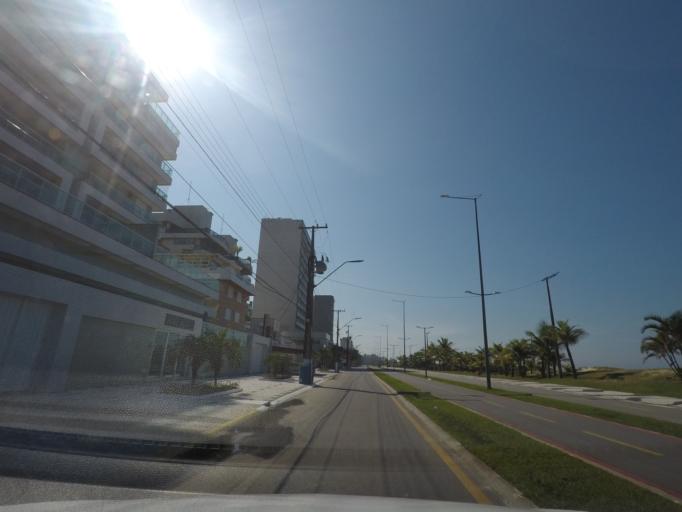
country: BR
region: Parana
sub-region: Guaratuba
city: Guaratuba
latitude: -25.8382
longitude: -48.5383
